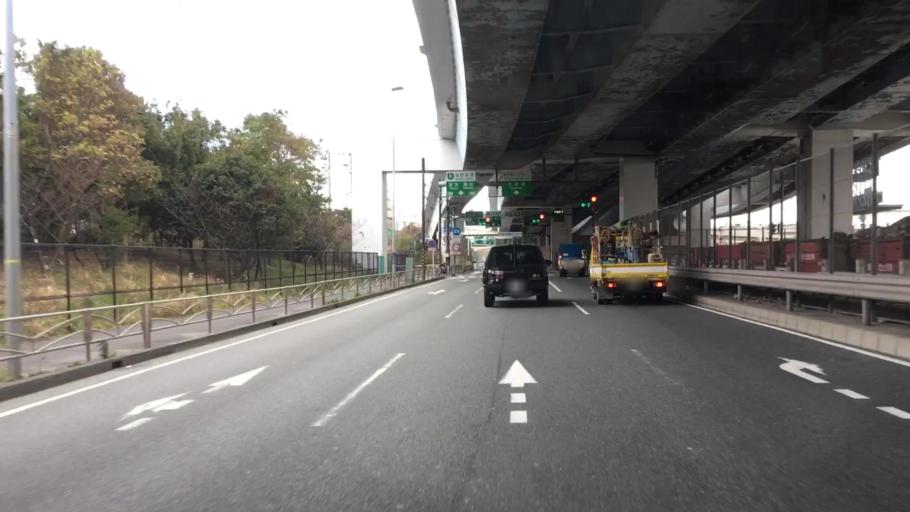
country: JP
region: Kanagawa
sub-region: Kawasaki-shi
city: Kawasaki
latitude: 35.5211
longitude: 139.7871
